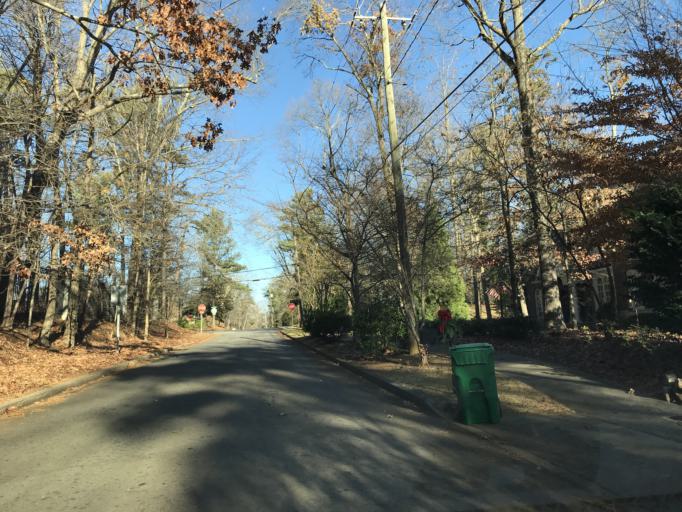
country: US
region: Georgia
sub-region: DeKalb County
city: North Atlanta
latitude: 33.8800
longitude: -84.3353
